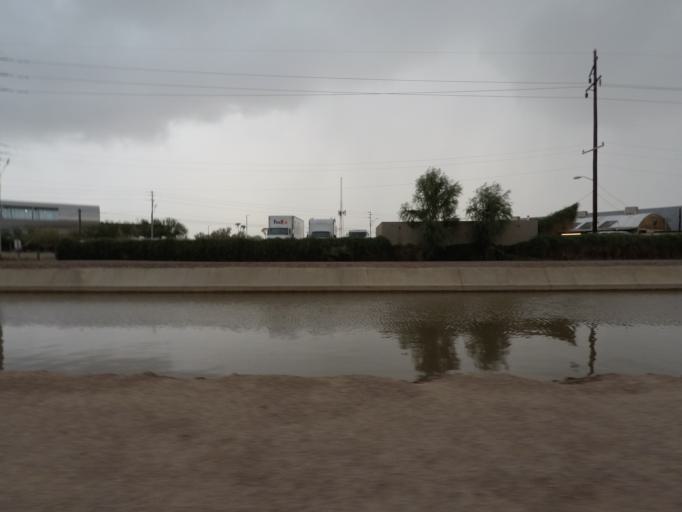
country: US
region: Arizona
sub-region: Maricopa County
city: Tempe Junction
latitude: 33.4487
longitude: -111.9911
